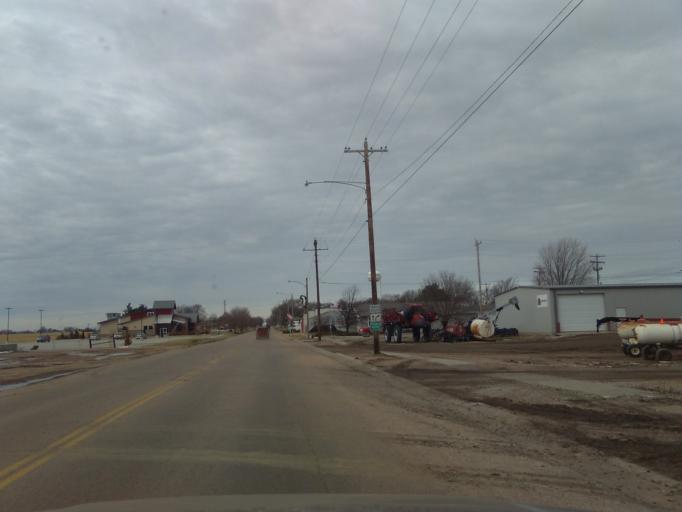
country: US
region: Nebraska
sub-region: Hall County
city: Grand Island
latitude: 40.7710
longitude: -98.3686
